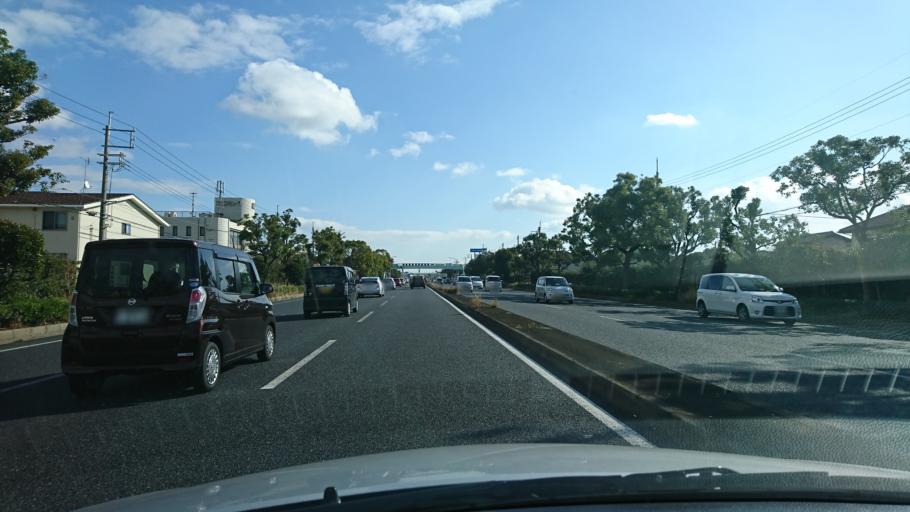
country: JP
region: Hyogo
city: Kakogawacho-honmachi
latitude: 34.7607
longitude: 134.8171
